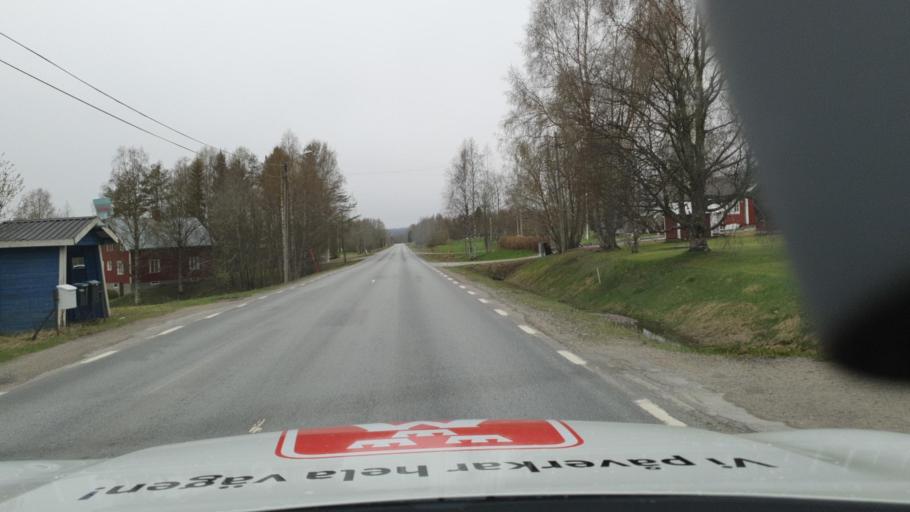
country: SE
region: Vaesterbotten
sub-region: Vannas Kommun
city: Vaennaes
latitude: 63.7728
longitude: 19.6834
